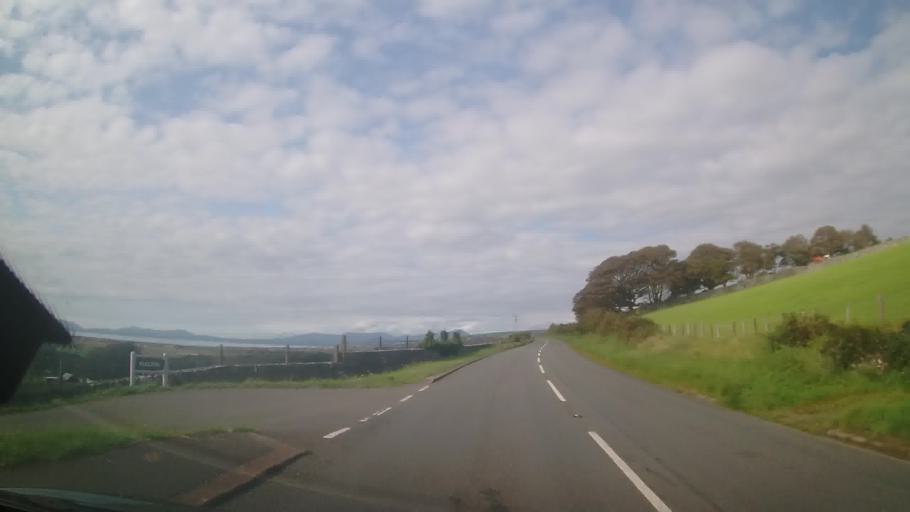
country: GB
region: Wales
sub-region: Gwynedd
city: Llanbedr
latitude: 52.8038
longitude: -4.1023
